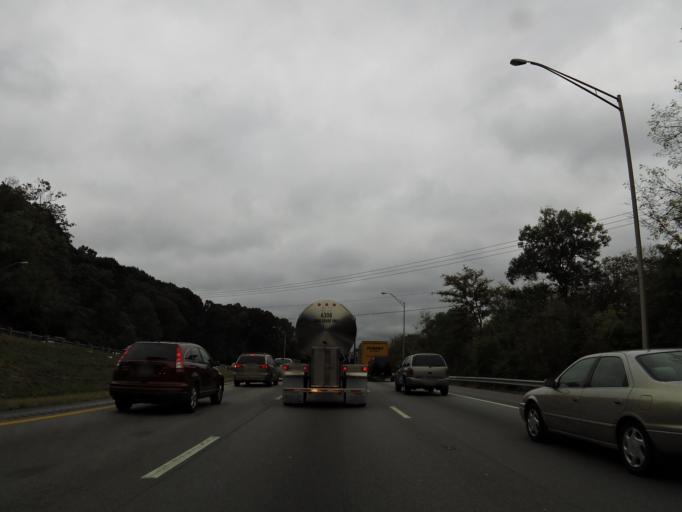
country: US
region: Tennessee
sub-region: Hamilton County
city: East Ridge
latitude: 35.0170
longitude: -85.2693
